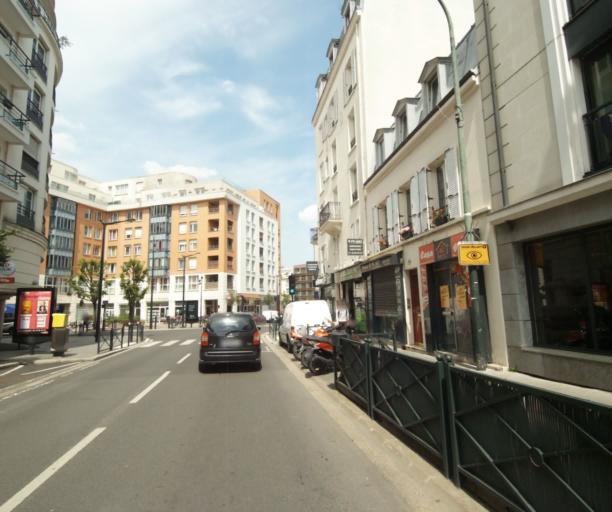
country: FR
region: Ile-de-France
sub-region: Departement des Hauts-de-Seine
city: Bois-Colombes
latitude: 48.9124
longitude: 2.2723
